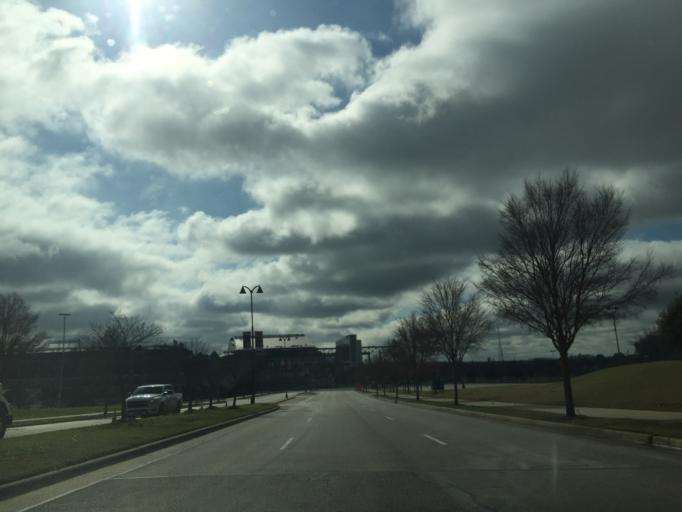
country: US
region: Texas
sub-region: Tarrant County
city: Arlington
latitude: 32.7572
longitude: -97.0854
